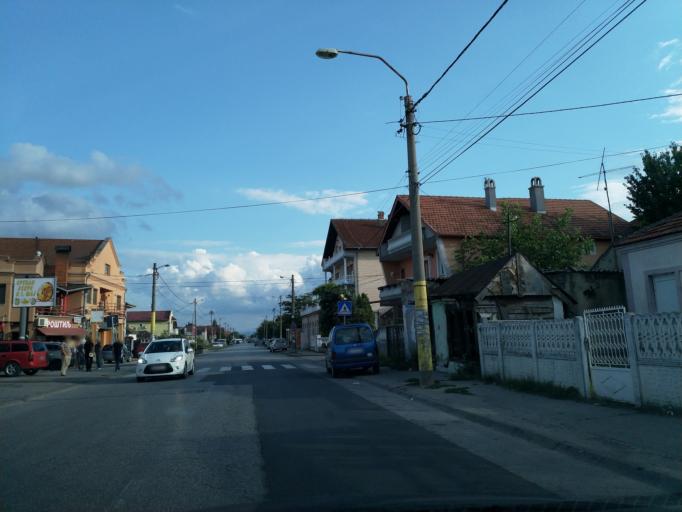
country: RS
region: Central Serbia
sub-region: Pomoravski Okrug
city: Paracin
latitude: 43.8511
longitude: 21.4133
